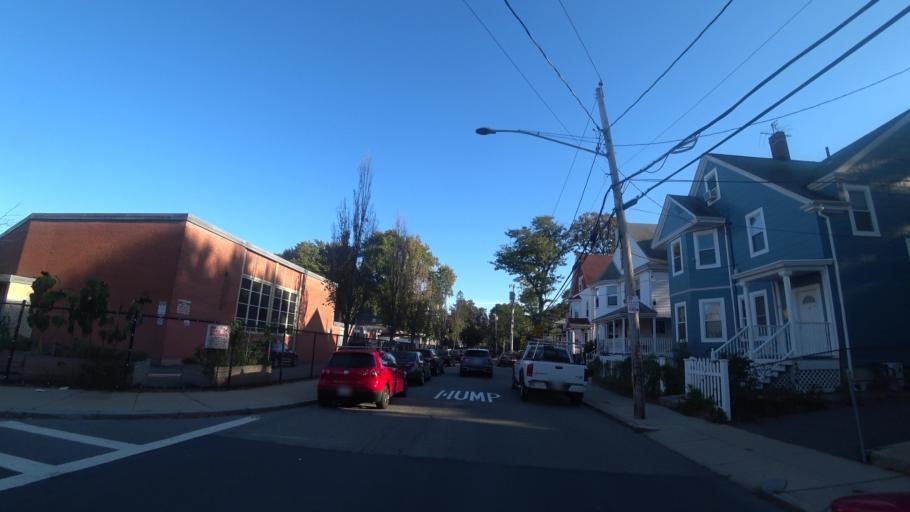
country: US
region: Massachusetts
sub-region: Norfolk County
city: Brookline
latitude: 42.3220
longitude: -71.1064
